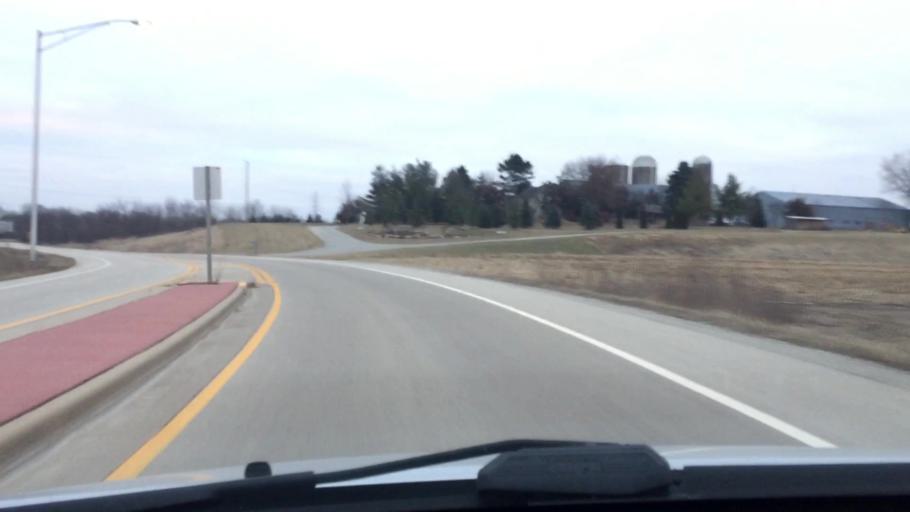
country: US
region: Wisconsin
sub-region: Jefferson County
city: Watertown
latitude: 43.1528
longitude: -88.7495
